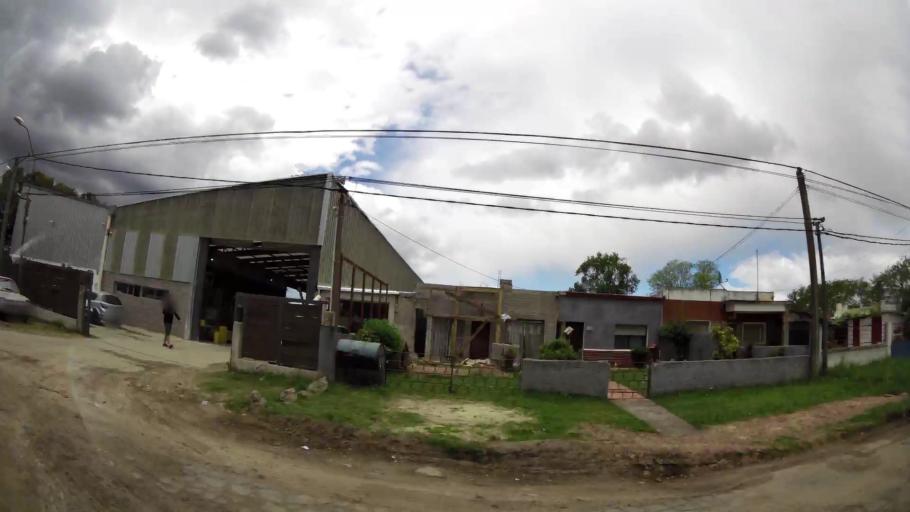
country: UY
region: Canelones
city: Toledo
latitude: -34.8025
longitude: -56.1355
